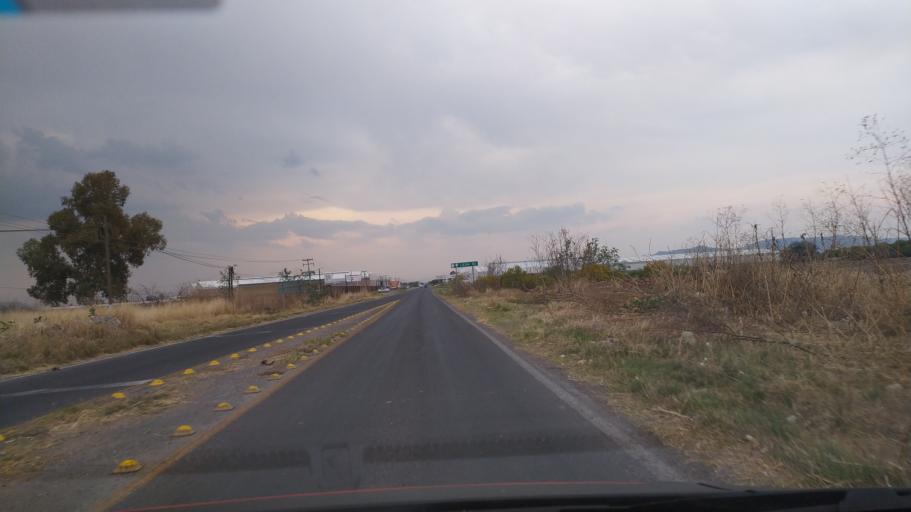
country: MX
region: Guanajuato
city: Ciudad Manuel Doblado
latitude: 20.7426
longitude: -101.9302
